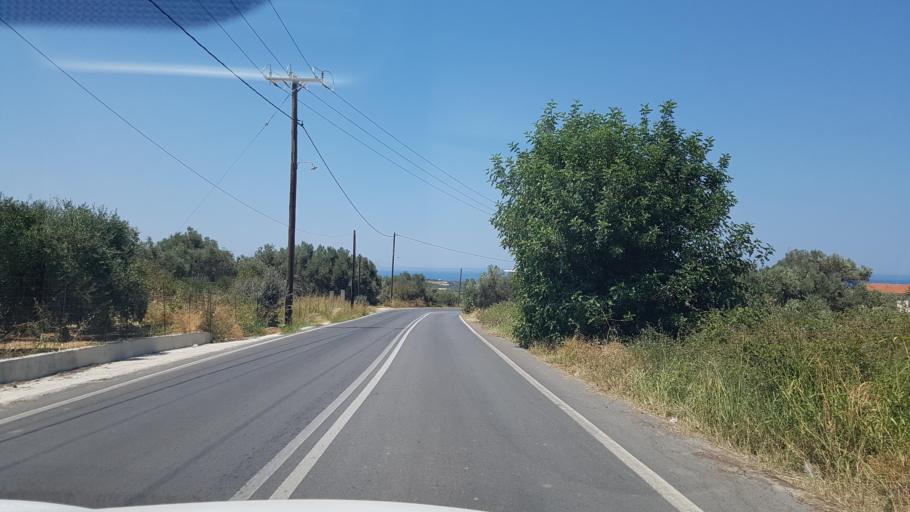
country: GR
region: Crete
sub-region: Nomos Rethymnis
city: Agia Foteini
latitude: 35.3515
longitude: 24.5901
